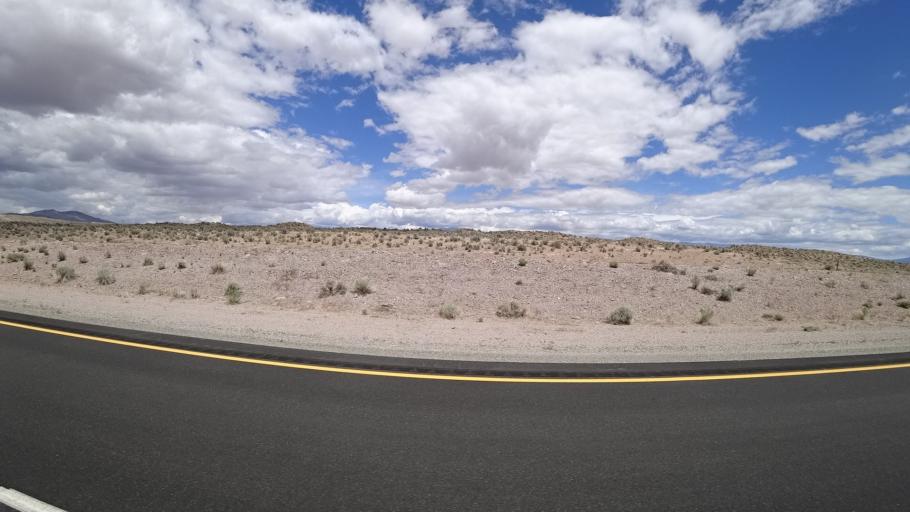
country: US
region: California
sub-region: Inyo County
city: West Bishop
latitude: 37.4256
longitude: -118.5595
